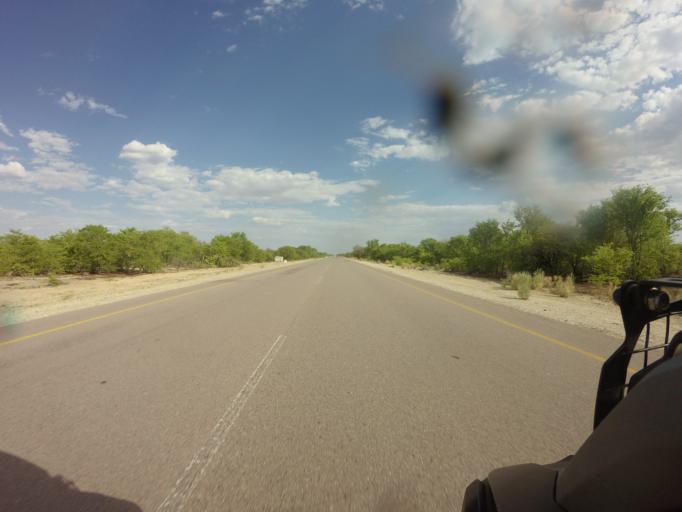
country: AO
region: Cunene
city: Ondjiva
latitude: -16.7744
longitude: 15.4021
